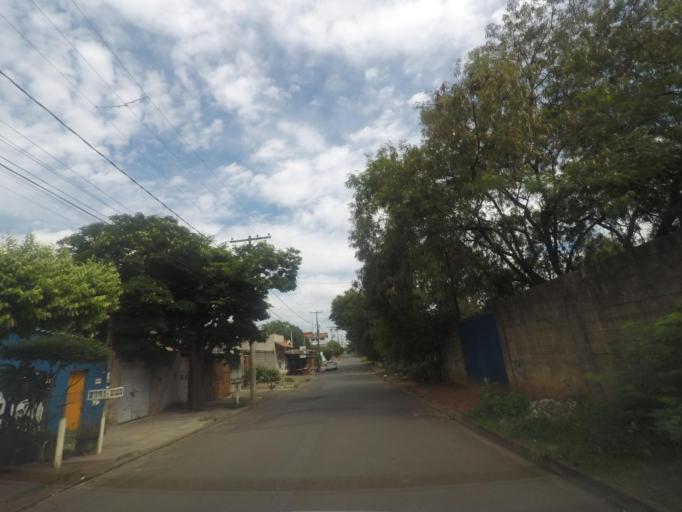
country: BR
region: Sao Paulo
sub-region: Sumare
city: Sumare
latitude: -22.8038
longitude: -47.2448
